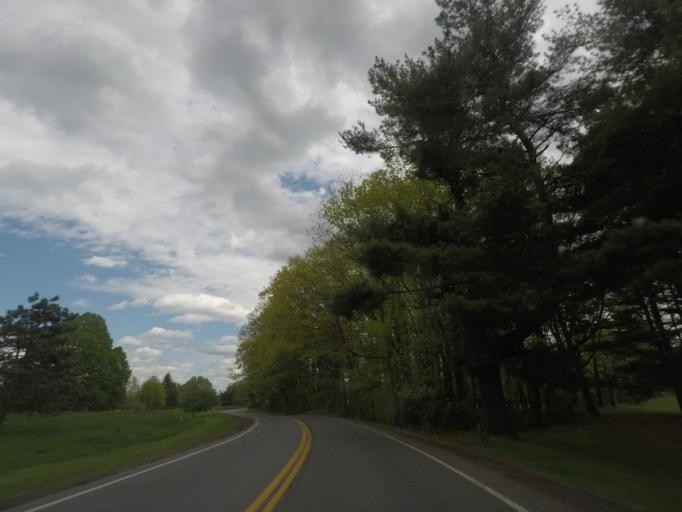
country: US
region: New York
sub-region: Albany County
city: Voorheesville
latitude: 42.6760
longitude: -73.9210
